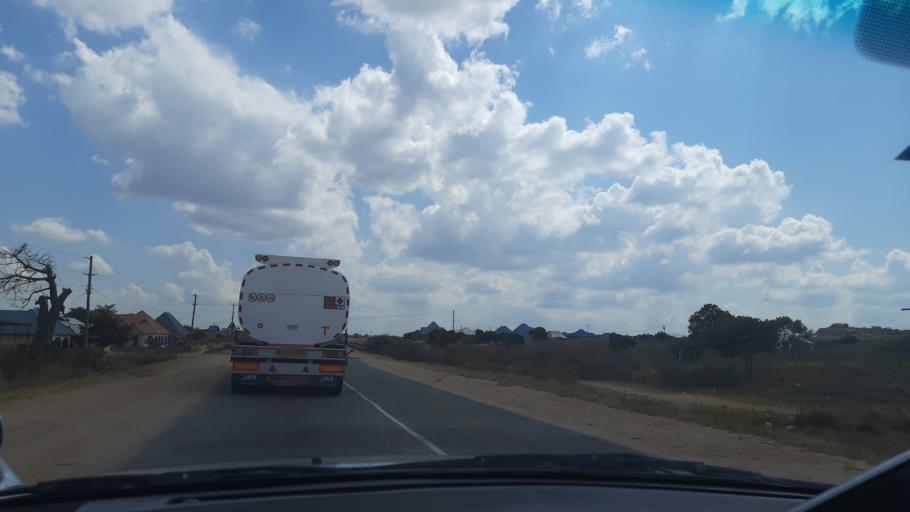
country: TZ
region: Dodoma
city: Dodoma
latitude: -6.0894
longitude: 35.6176
